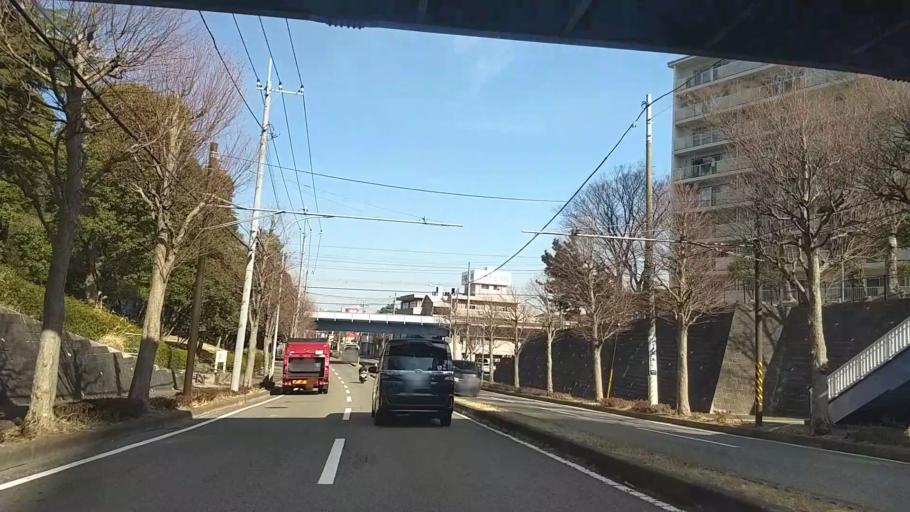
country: JP
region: Kanagawa
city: Kamakura
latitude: 35.3750
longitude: 139.5819
